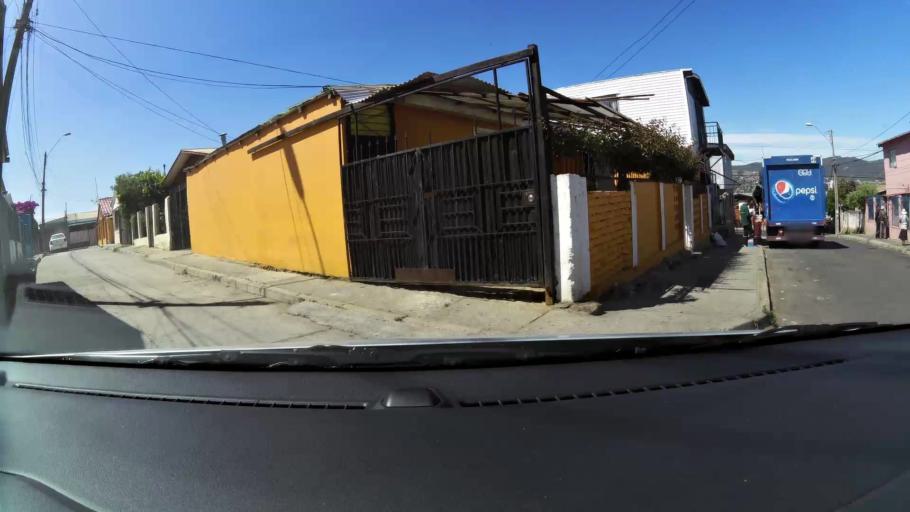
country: CL
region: Valparaiso
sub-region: Provincia de Valparaiso
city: Vina del Mar
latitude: -33.0533
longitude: -71.5791
